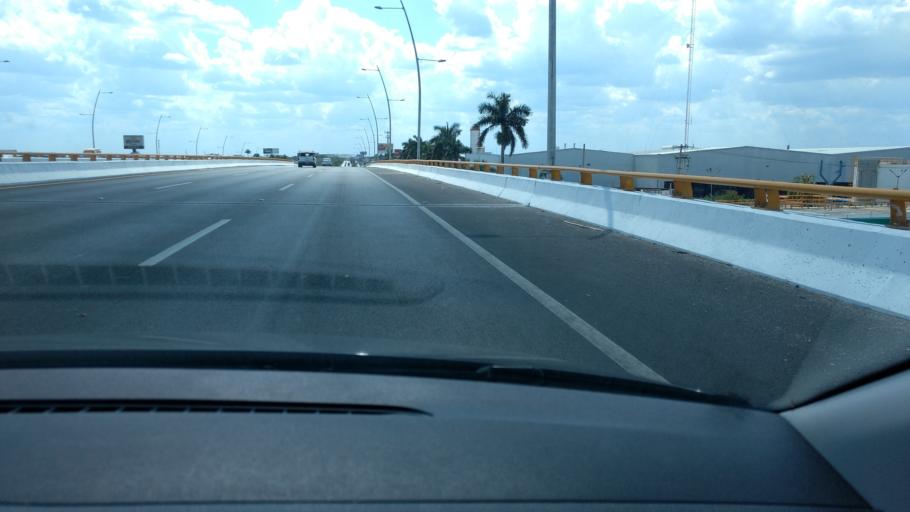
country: MX
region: Yucatan
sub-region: Kanasin
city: Kanasin
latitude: 20.9709
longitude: -89.5651
